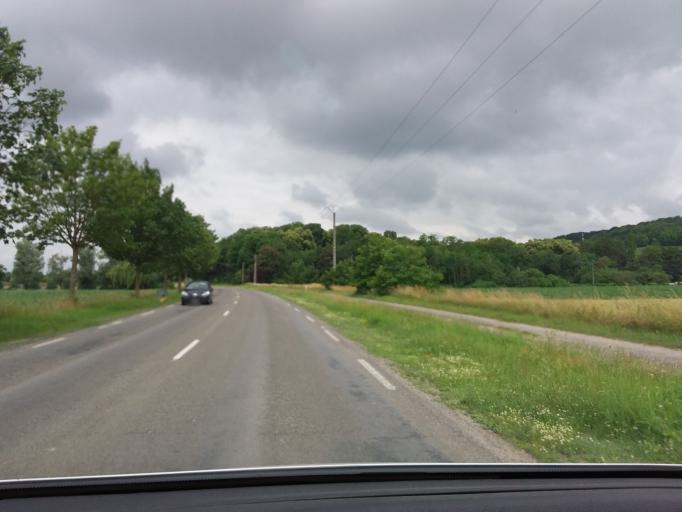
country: FR
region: Picardie
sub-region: Departement de l'Aisne
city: Bucy-le-Long
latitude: 49.3890
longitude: 3.3892
